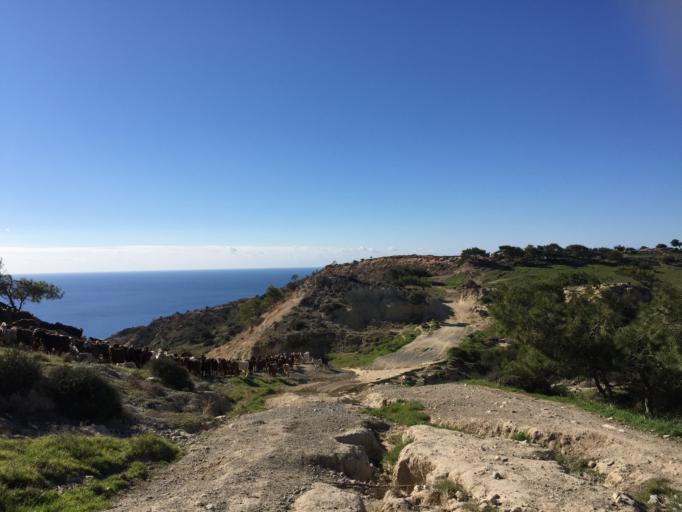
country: CY
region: Limassol
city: Pissouri
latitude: 34.6609
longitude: 32.6782
